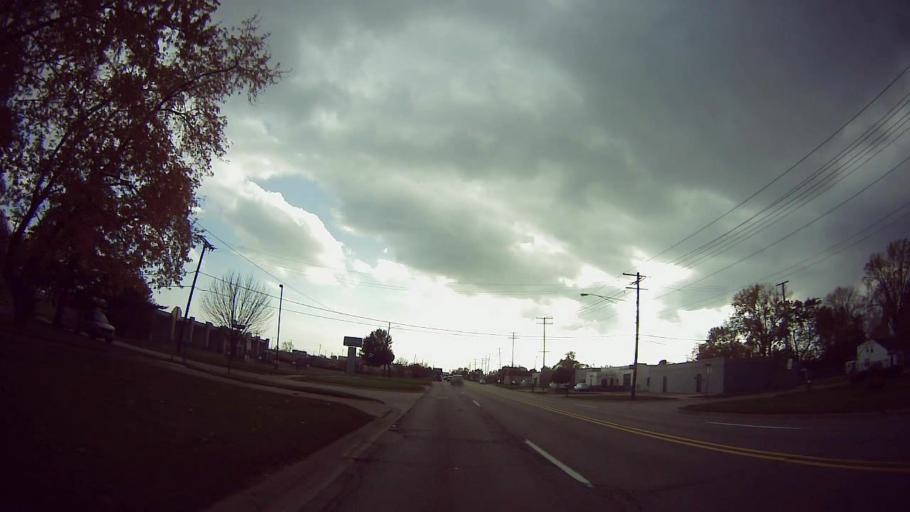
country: US
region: Michigan
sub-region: Macomb County
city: Warren
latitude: 42.4672
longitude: -83.0058
